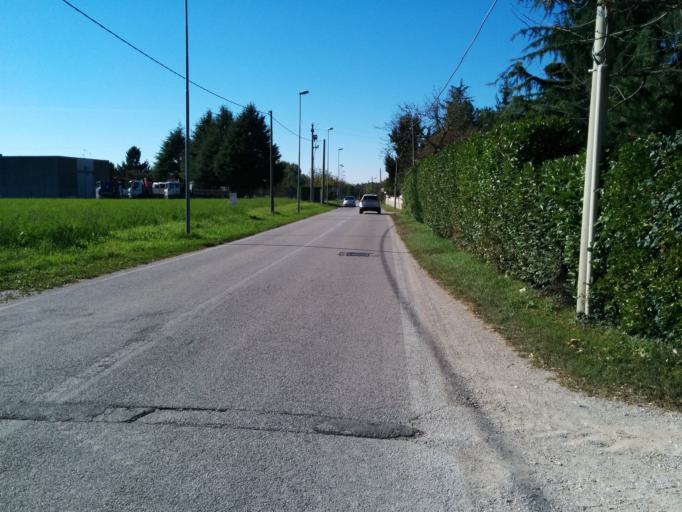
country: IT
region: Friuli Venezia Giulia
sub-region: Provincia di Udine
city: Pagnacco
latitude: 46.1144
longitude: 13.2012
